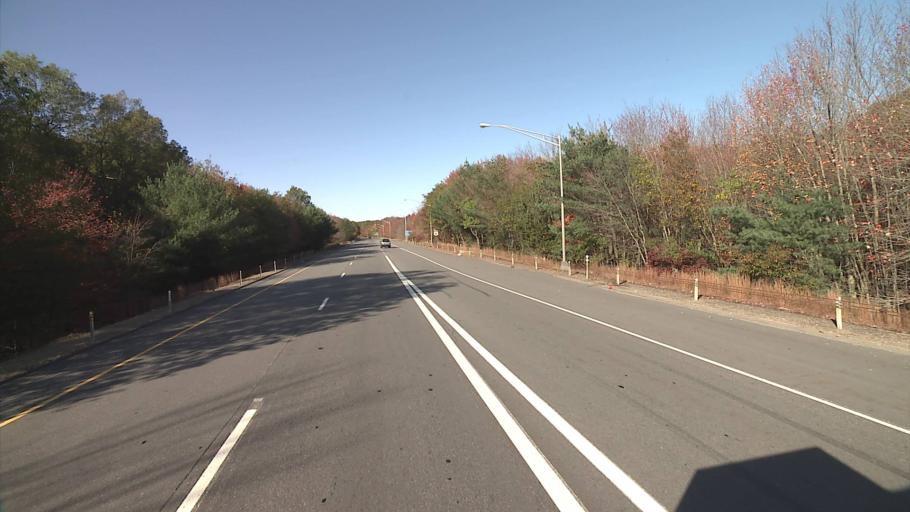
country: US
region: Connecticut
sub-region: Windham County
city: Willimantic
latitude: 41.7307
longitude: -72.2202
